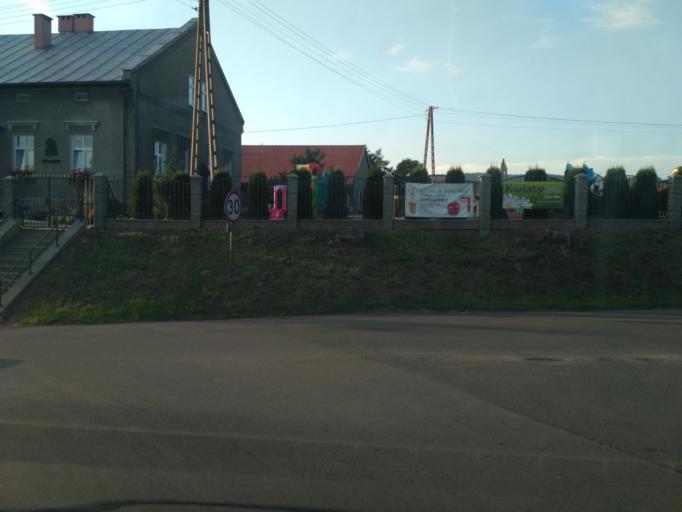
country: PL
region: Subcarpathian Voivodeship
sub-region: Powiat krosnienski
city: Korczyna
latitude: 49.7130
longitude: 21.8142
